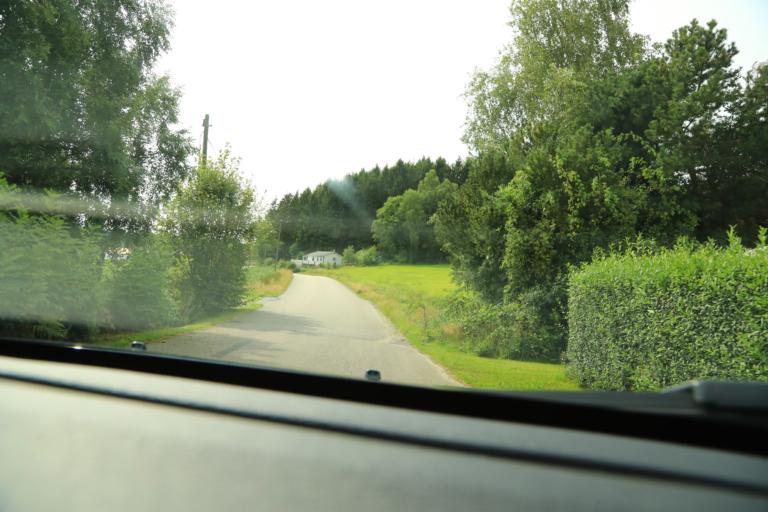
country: SE
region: Halland
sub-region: Varbergs Kommun
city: Varberg
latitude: 57.1873
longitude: 12.2505
